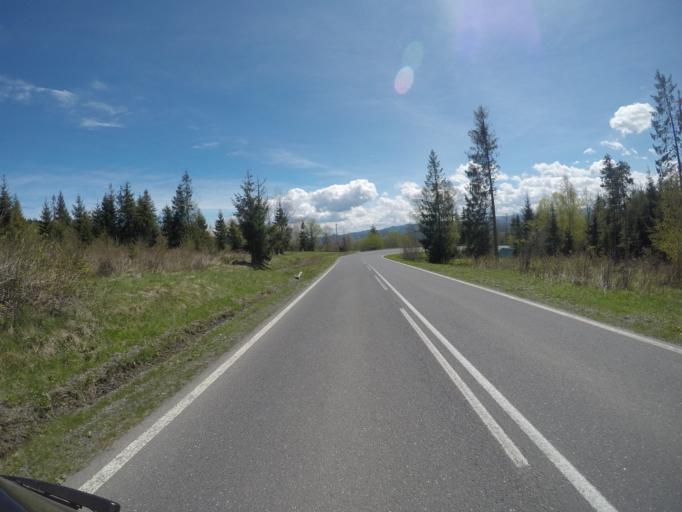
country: SK
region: Presovsky
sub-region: Okres Poprad
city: Strba
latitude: 49.0978
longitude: 20.0690
